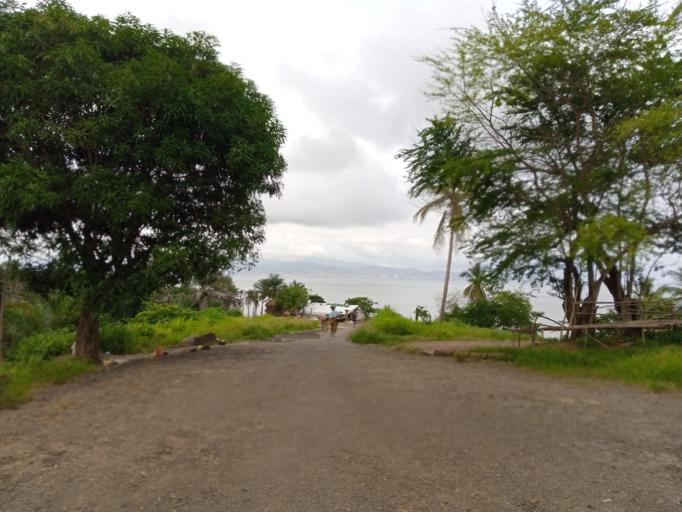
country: SL
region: Northern Province
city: Masoyila
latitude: 8.5857
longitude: -13.2000
